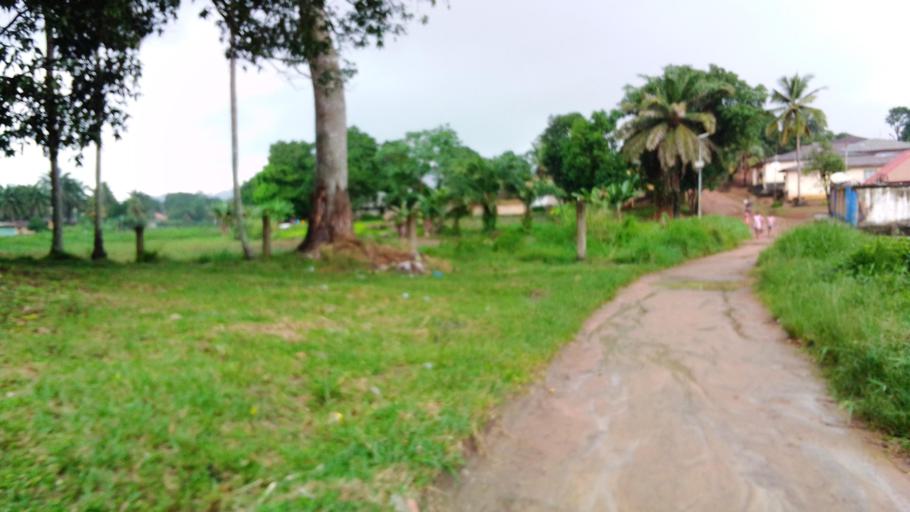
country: SL
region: Eastern Province
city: Kenema
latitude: 7.8792
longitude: -11.1769
